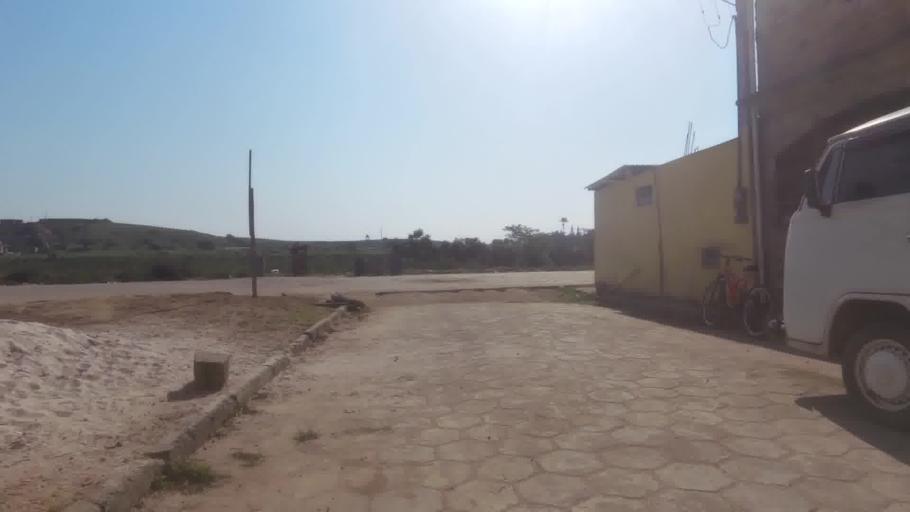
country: BR
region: Espirito Santo
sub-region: Itapemirim
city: Itapemirim
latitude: -21.0157
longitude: -40.8161
